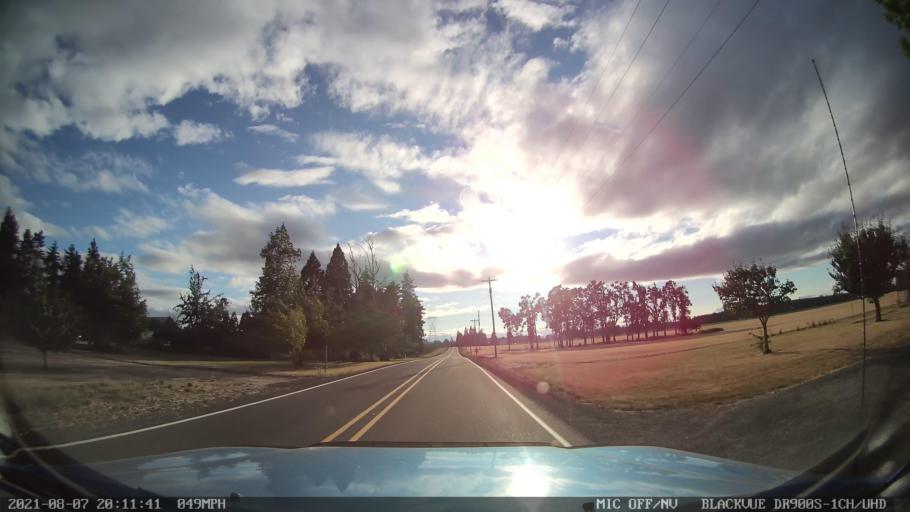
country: US
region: Oregon
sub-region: Marion County
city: Hayesville
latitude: 44.9583
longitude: -122.8948
